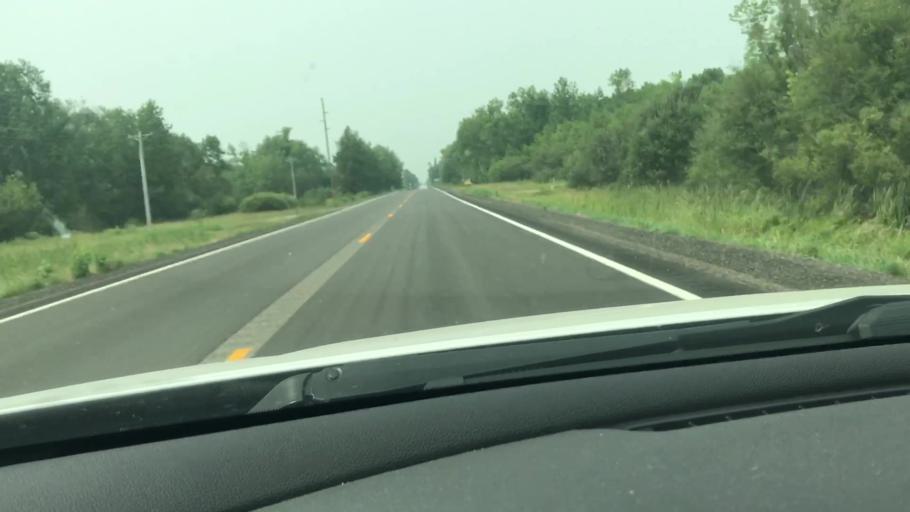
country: US
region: Minnesota
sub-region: Itasca County
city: Cohasset
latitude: 47.3643
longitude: -93.8723
